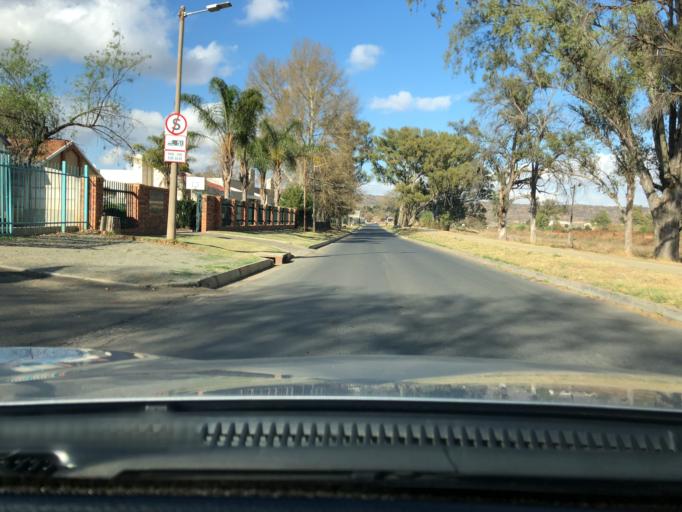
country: ZA
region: KwaZulu-Natal
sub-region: uThukela District Municipality
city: Ladysmith
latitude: -28.5620
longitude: 29.7775
